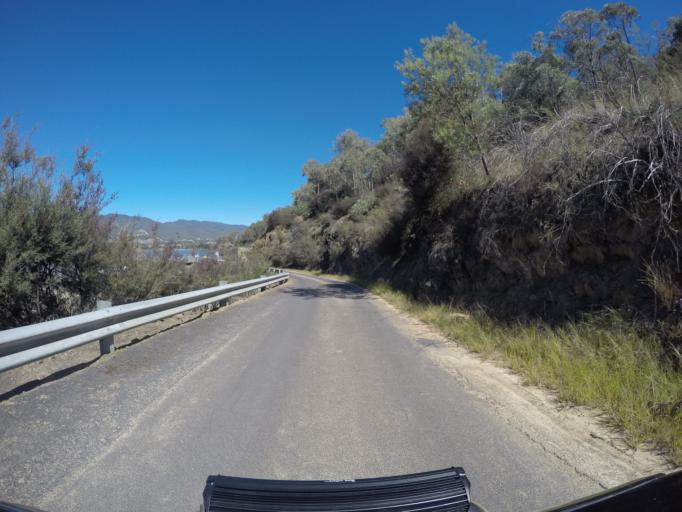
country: AU
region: New South Wales
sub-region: Snowy River
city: Jindabyne
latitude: -36.2202
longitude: 148.1076
